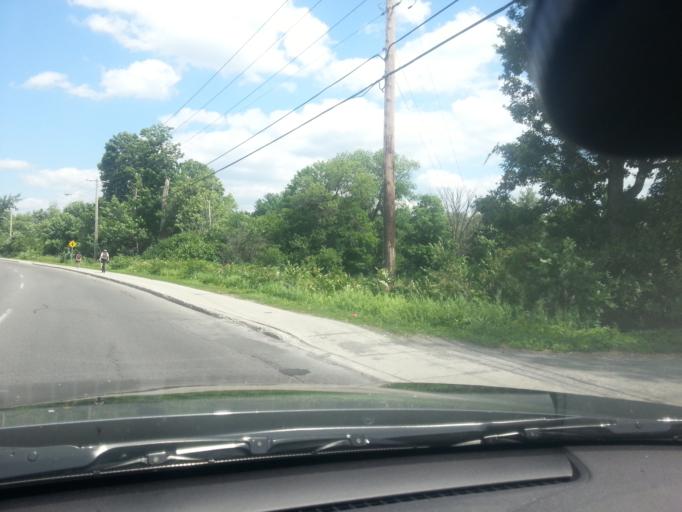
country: CA
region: Ontario
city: Bells Corners
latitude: 45.3969
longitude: -75.8163
